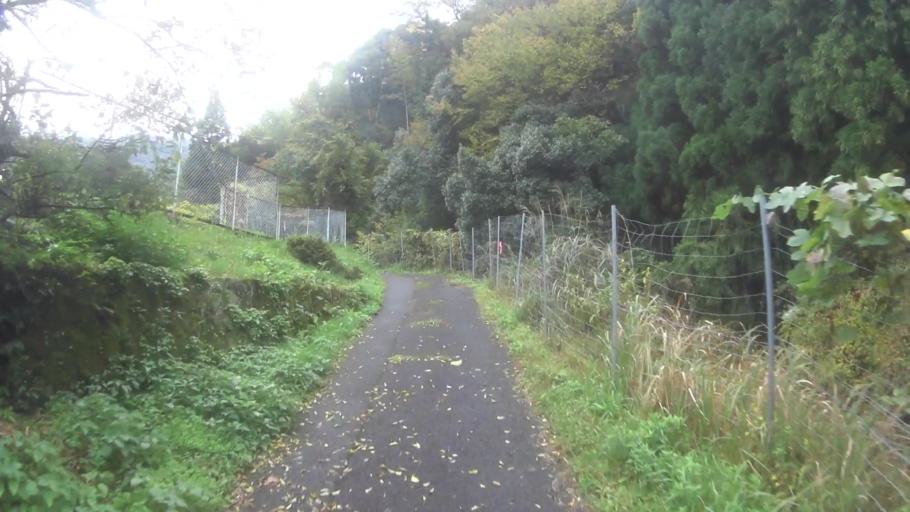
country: JP
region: Kyoto
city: Miyazu
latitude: 35.4914
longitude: 135.1205
